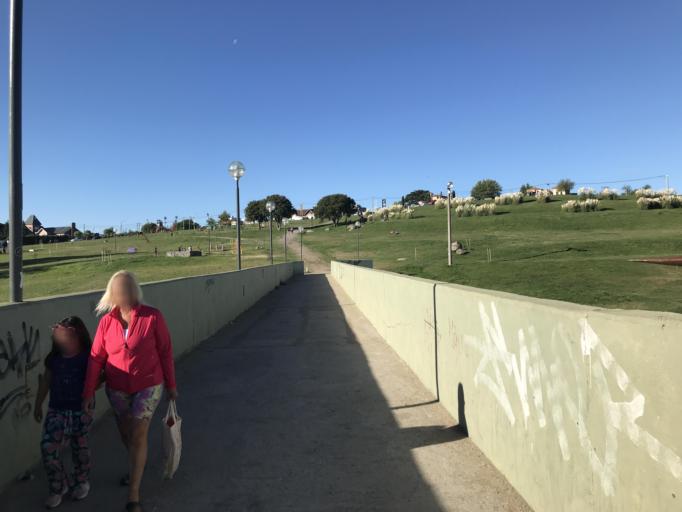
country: AR
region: Buenos Aires
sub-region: Partido de Tandil
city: Tandil
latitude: -37.3373
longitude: -59.1143
